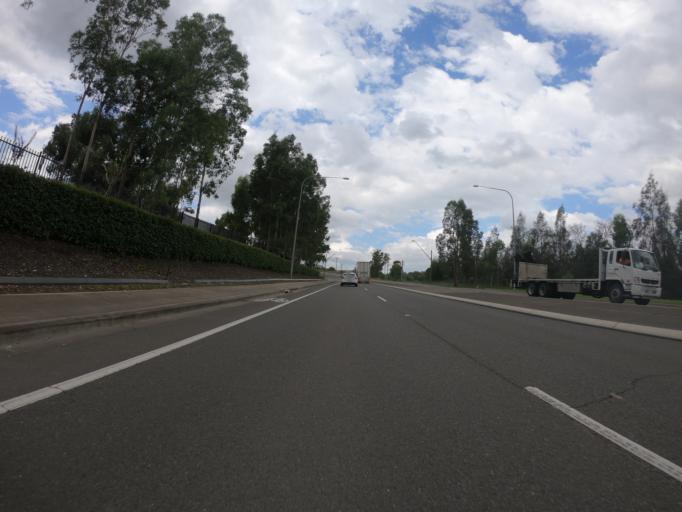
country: AU
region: New South Wales
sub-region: Blacktown
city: Mount Druitt
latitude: -33.8142
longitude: 150.7831
